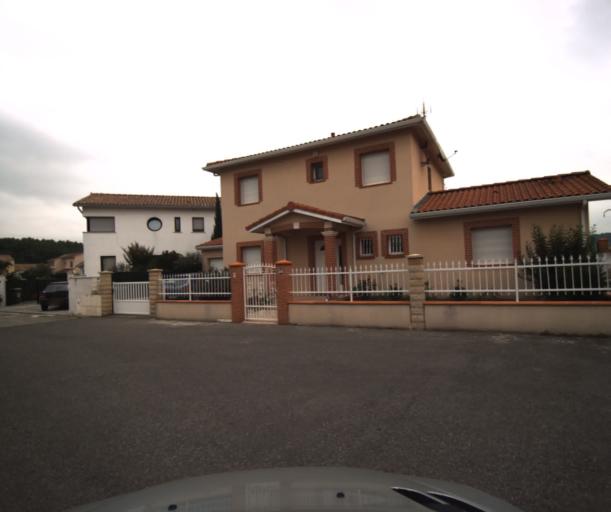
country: FR
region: Midi-Pyrenees
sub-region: Departement de la Haute-Garonne
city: Portet-sur-Garonne
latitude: 43.5361
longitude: 1.4153
